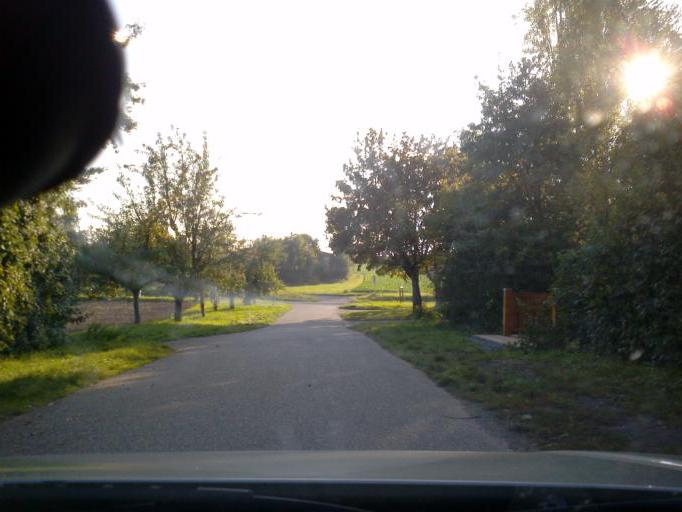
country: DE
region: Baden-Wuerttemberg
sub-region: Regierungsbezirk Stuttgart
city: Brackenheim
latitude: 49.0975
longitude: 9.0687
